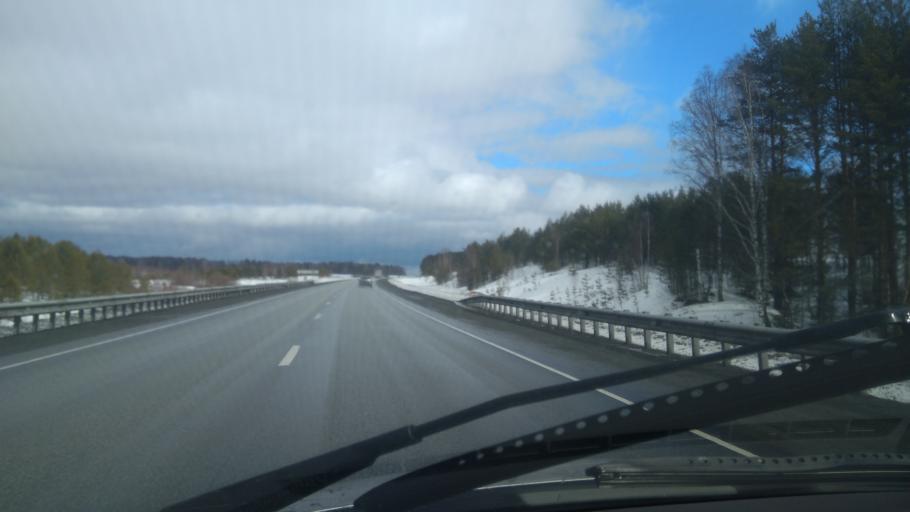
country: RU
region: Sverdlovsk
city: Bisert'
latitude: 56.8061
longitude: 58.7191
